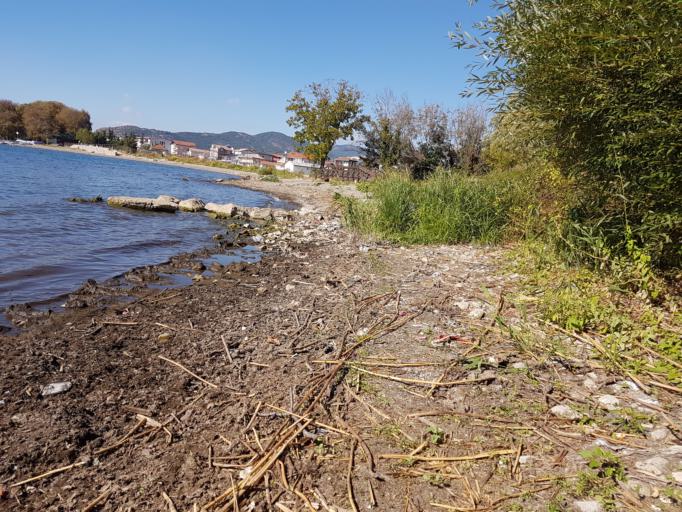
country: MK
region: Ohrid
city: Ohrid
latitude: 41.1163
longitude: 20.7882
